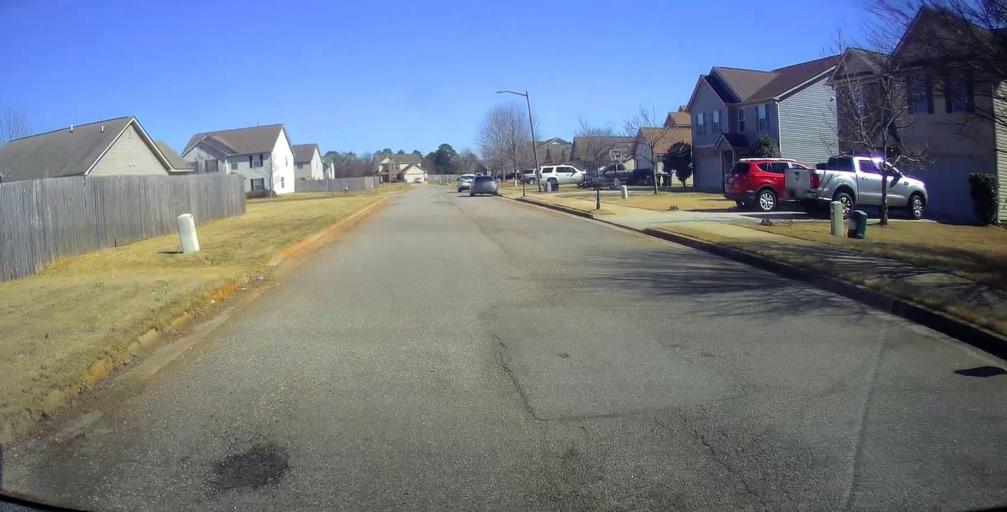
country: US
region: Georgia
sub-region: Houston County
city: Centerville
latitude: 32.6438
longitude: -83.7117
